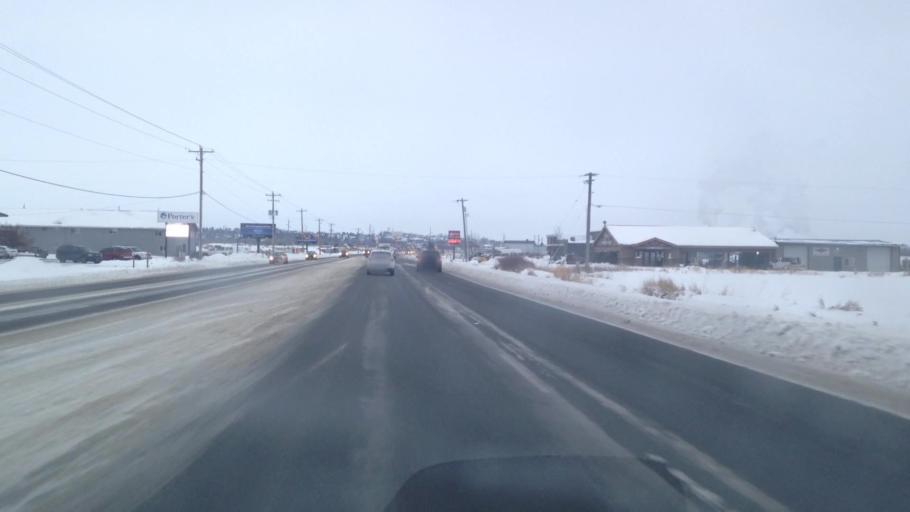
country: US
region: Idaho
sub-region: Madison County
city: Rexburg
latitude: 43.8486
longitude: -111.7780
